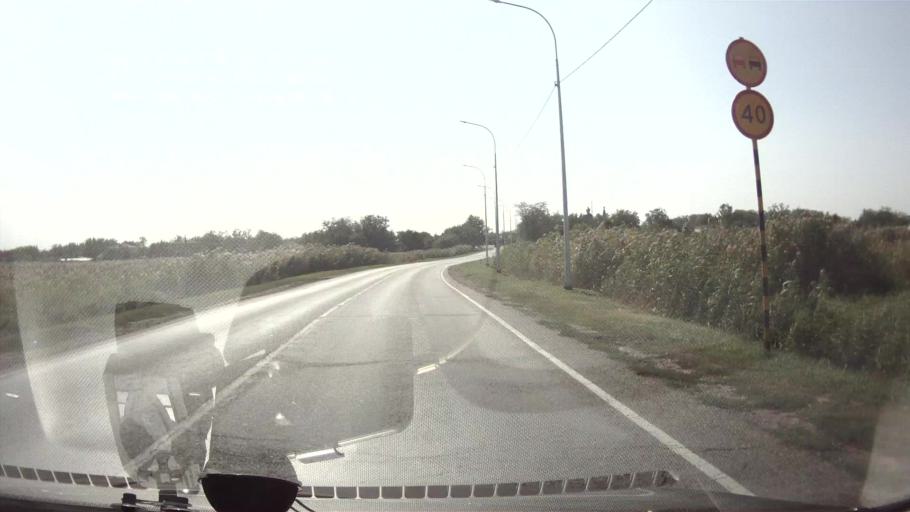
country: RU
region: Krasnodarskiy
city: Dmitriyevskaya
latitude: 45.7271
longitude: 40.7202
